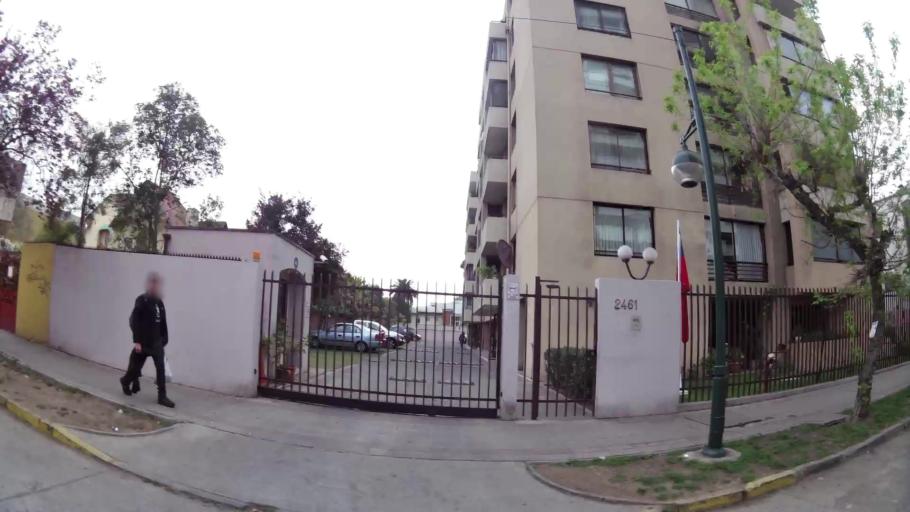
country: CL
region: Santiago Metropolitan
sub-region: Provincia de Santiago
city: Villa Presidente Frei, Nunoa, Santiago, Chile
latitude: -33.4505
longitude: -70.6131
